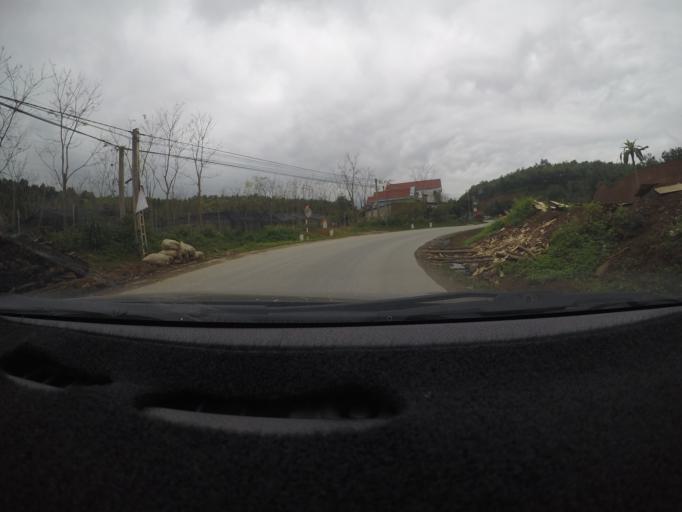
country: VN
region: Yen Bai
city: Co Phuc
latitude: 21.9215
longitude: 104.8021
